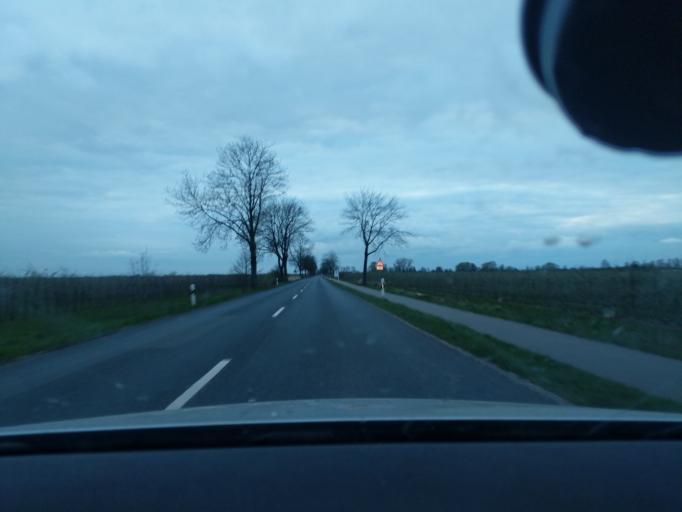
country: DE
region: Lower Saxony
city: Neu Wulmstorf
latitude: 53.5213
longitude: 9.7704
